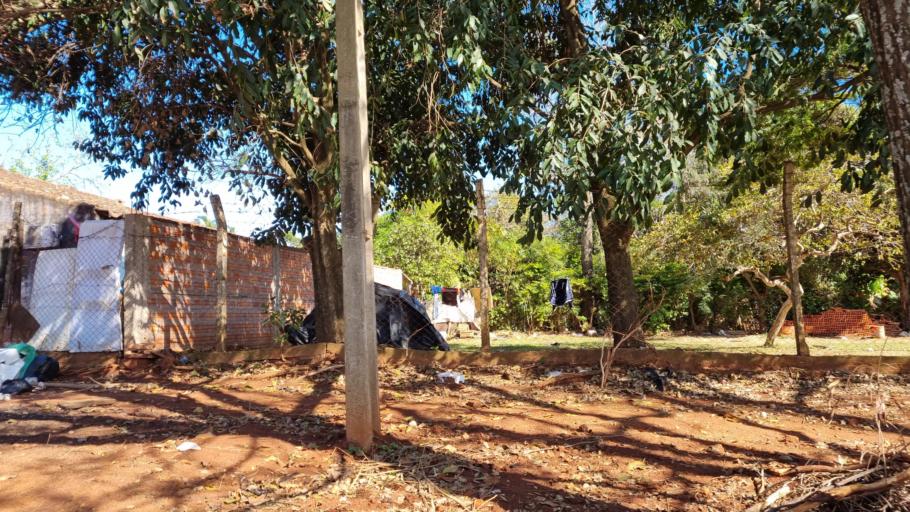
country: PY
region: Misiones
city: San Juan Bautista
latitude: -26.6673
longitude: -57.1410
